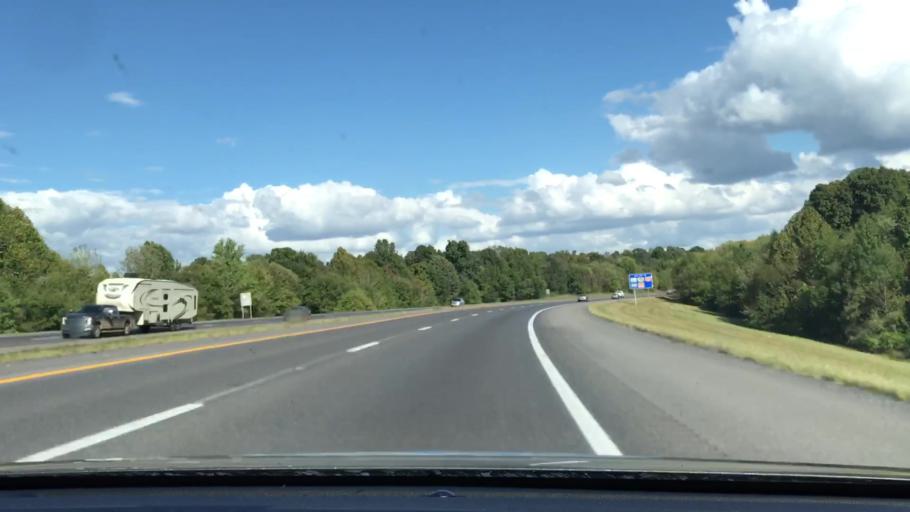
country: US
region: Kentucky
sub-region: Lyon County
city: Eddyville
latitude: 37.0755
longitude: -88.1355
